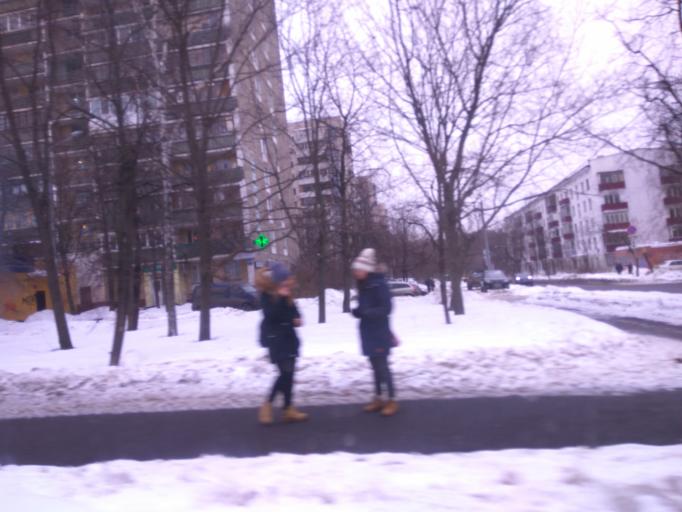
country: RU
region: Moskovskaya
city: Izmaylovo
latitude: 55.7969
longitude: 37.8191
